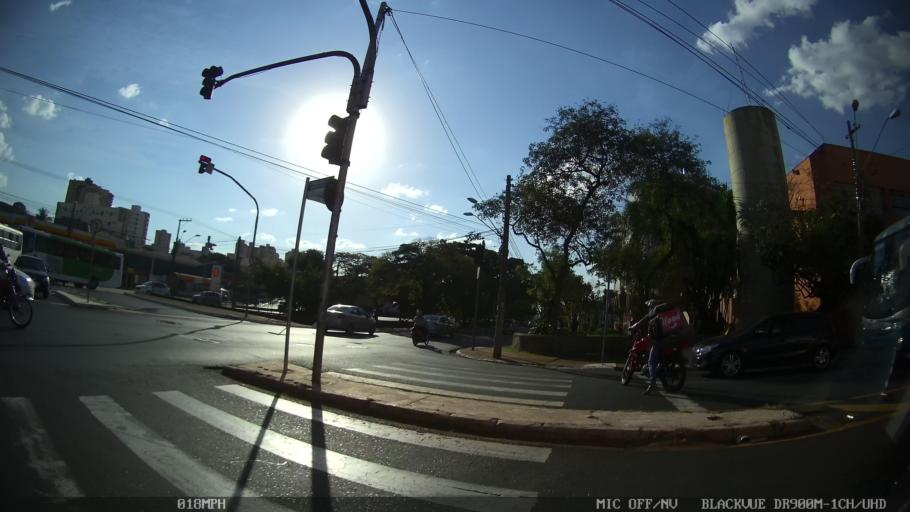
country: BR
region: Sao Paulo
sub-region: Ribeirao Preto
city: Ribeirao Preto
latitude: -21.1886
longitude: -47.7977
